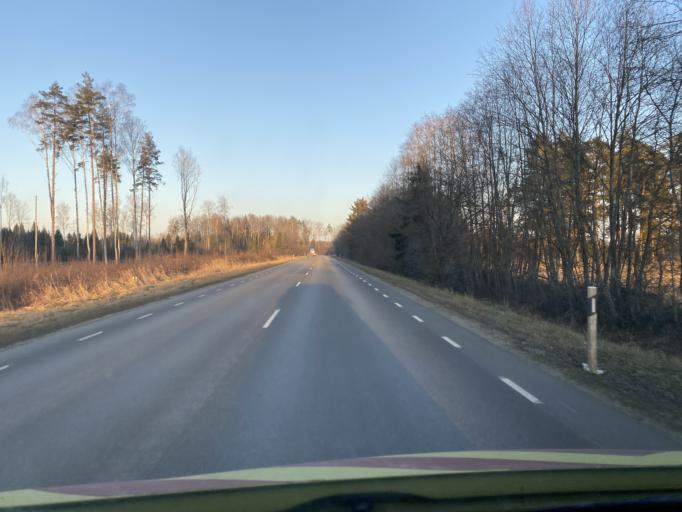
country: EE
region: Raplamaa
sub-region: Rapla vald
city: Rapla
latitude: 58.9626
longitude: 24.7077
